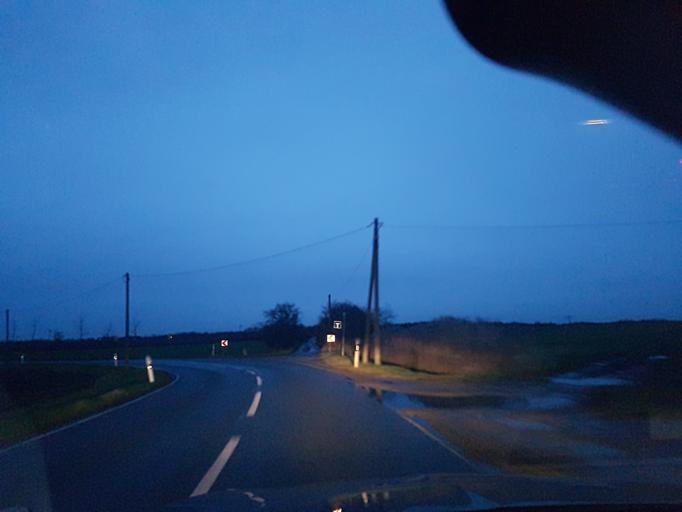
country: DE
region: Brandenburg
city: Doberlug-Kirchhain
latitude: 51.6148
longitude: 13.5878
